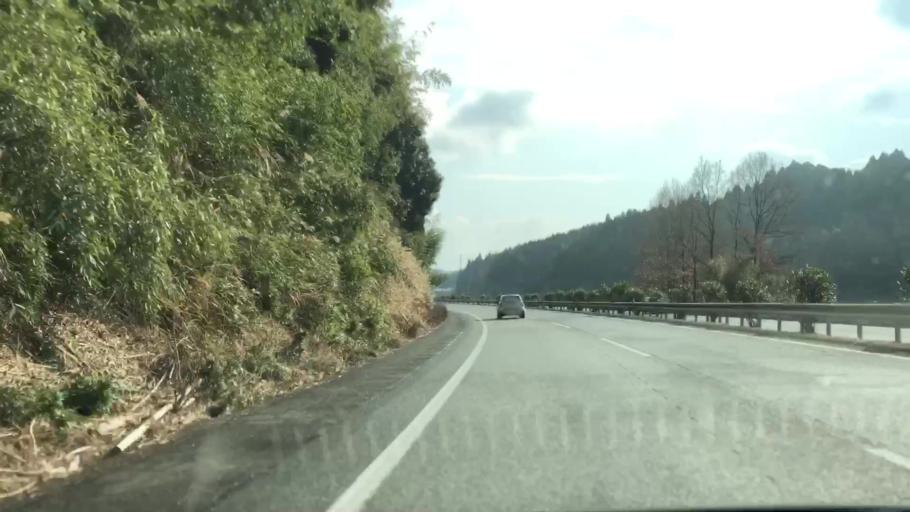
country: JP
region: Kumamoto
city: Yamaga
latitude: 33.0243
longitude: 130.5776
